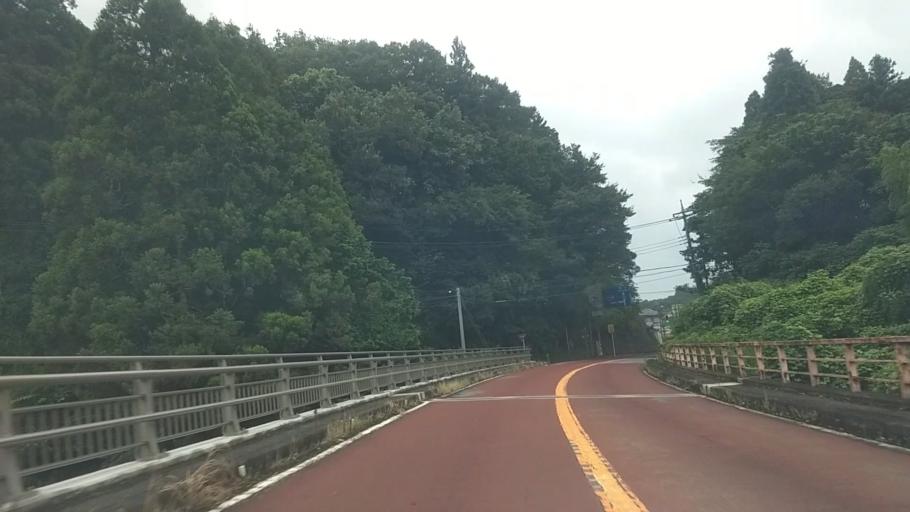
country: JP
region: Chiba
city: Kawaguchi
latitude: 35.2490
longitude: 140.0766
